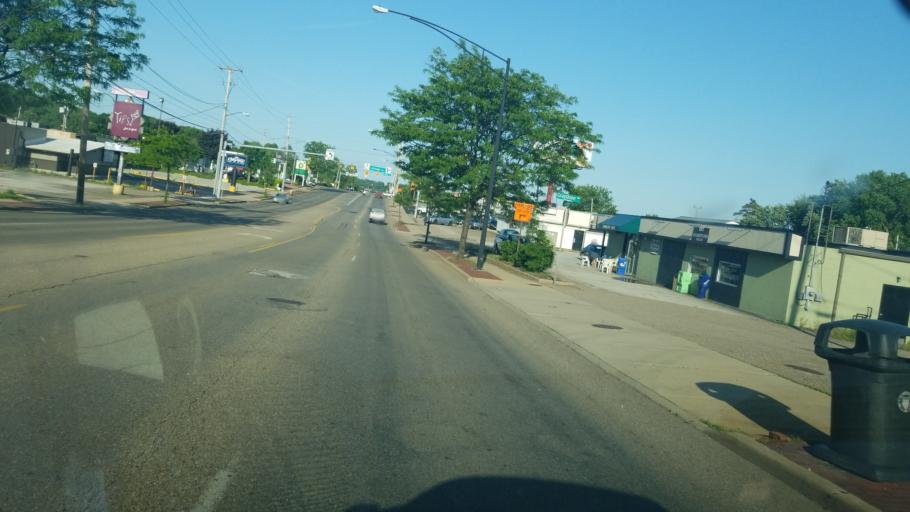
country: US
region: Ohio
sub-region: Summit County
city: Tallmadge
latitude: 41.1019
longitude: -81.4689
